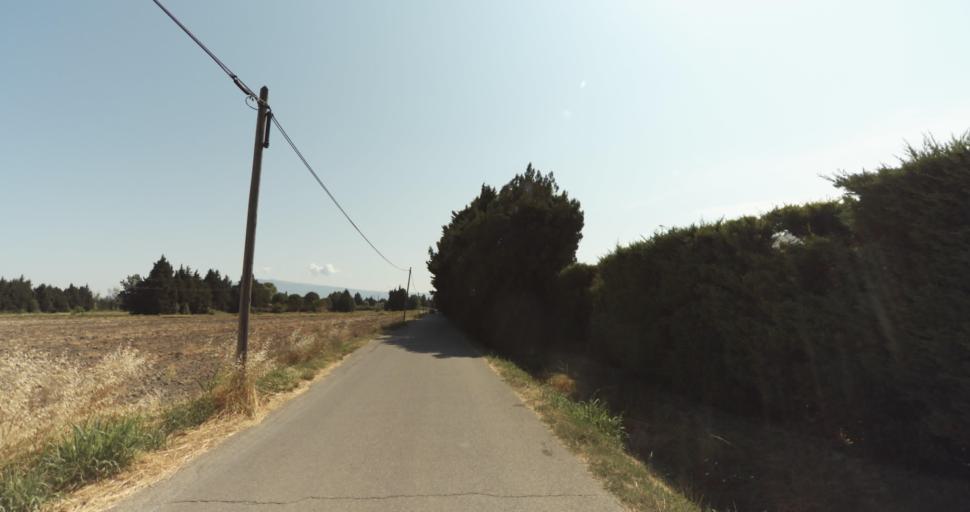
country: FR
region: Provence-Alpes-Cote d'Azur
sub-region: Departement du Vaucluse
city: Althen-des-Paluds
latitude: 44.0135
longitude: 4.9791
